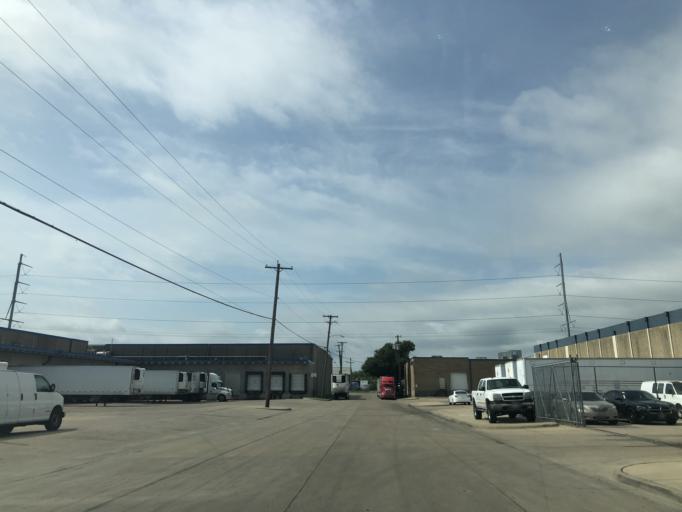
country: US
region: Texas
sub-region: Dallas County
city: Irving
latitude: 32.8098
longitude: -96.8779
